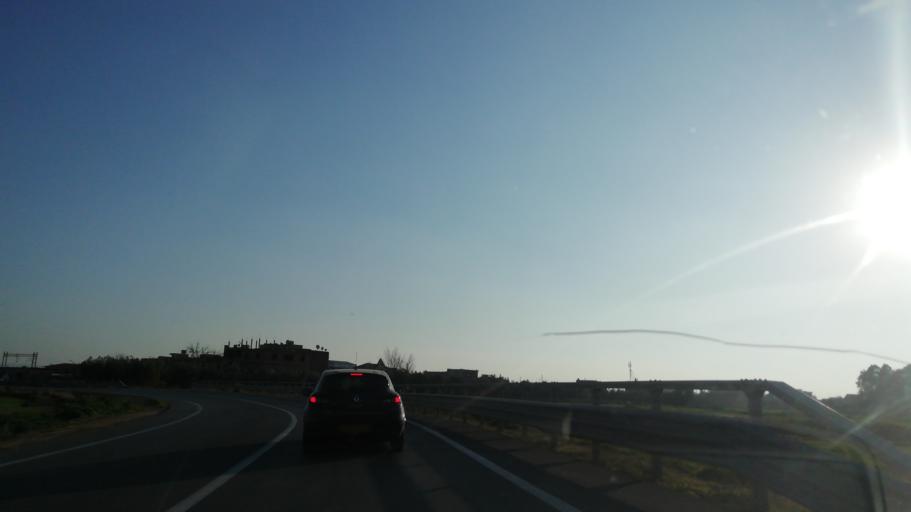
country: DZ
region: Sidi Bel Abbes
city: Sidi Bel Abbes
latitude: 35.1687
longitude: -0.6876
